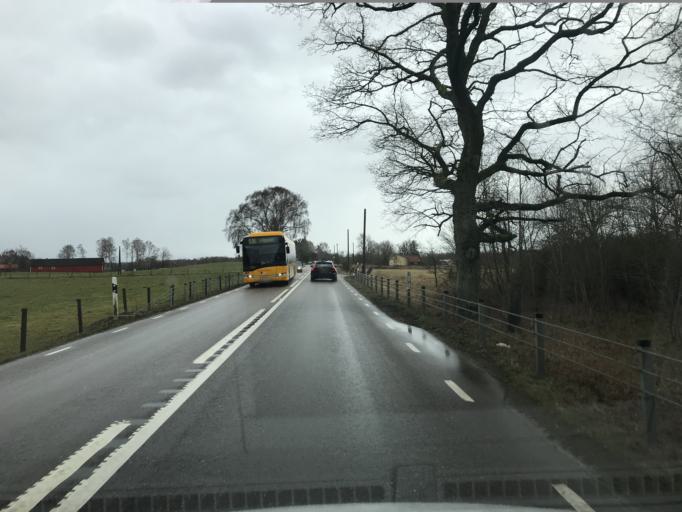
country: SE
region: Skane
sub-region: Klippans Kommun
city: Ljungbyhed
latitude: 56.0984
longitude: 13.1819
